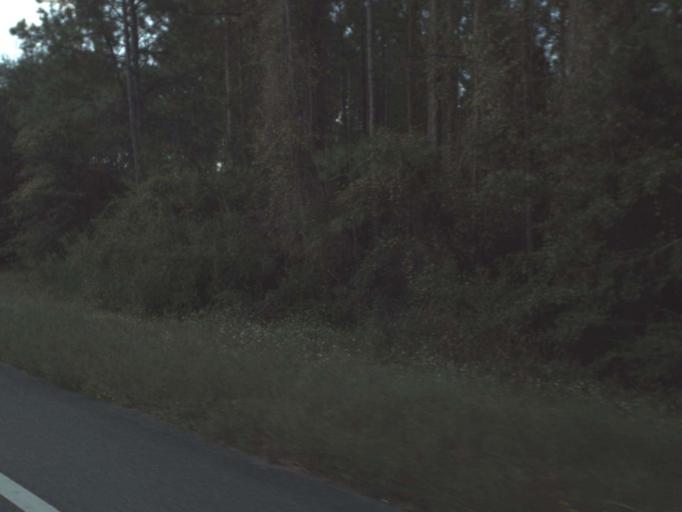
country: US
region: Florida
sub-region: Bay County
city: Laguna Beach
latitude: 30.4414
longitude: -85.8191
